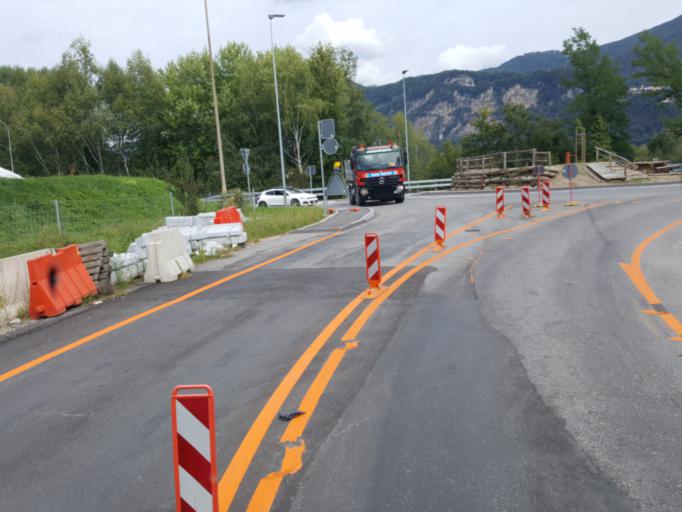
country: CH
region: Ticino
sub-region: Mendrisio District
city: Ligornetto
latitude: 45.8651
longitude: 8.9660
